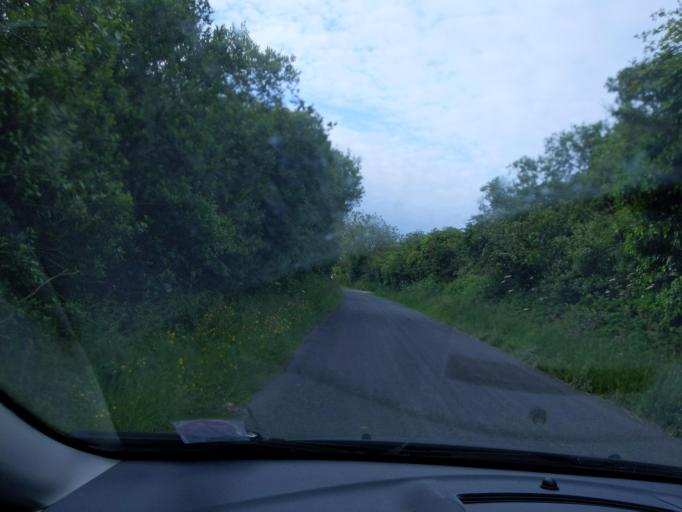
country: IM
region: Ramsey
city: Ramsey
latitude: 54.3838
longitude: -4.4496
